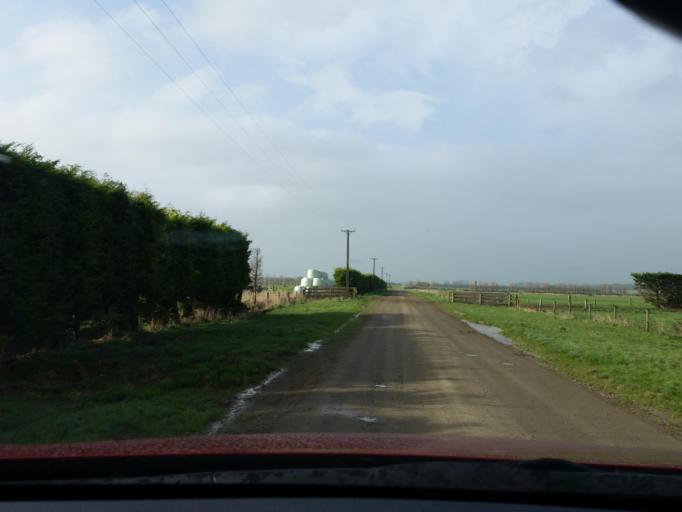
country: NZ
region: Southland
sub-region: Invercargill City
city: Invercargill
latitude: -46.3075
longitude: 168.4099
